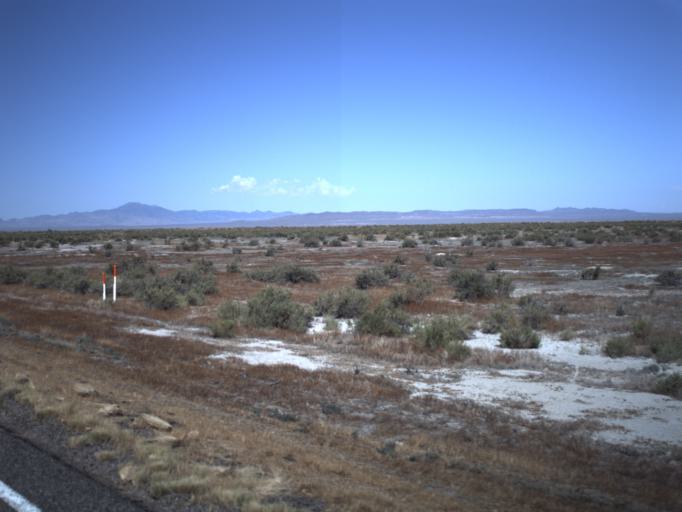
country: US
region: Utah
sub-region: Millard County
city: Delta
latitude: 39.3139
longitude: -112.7578
